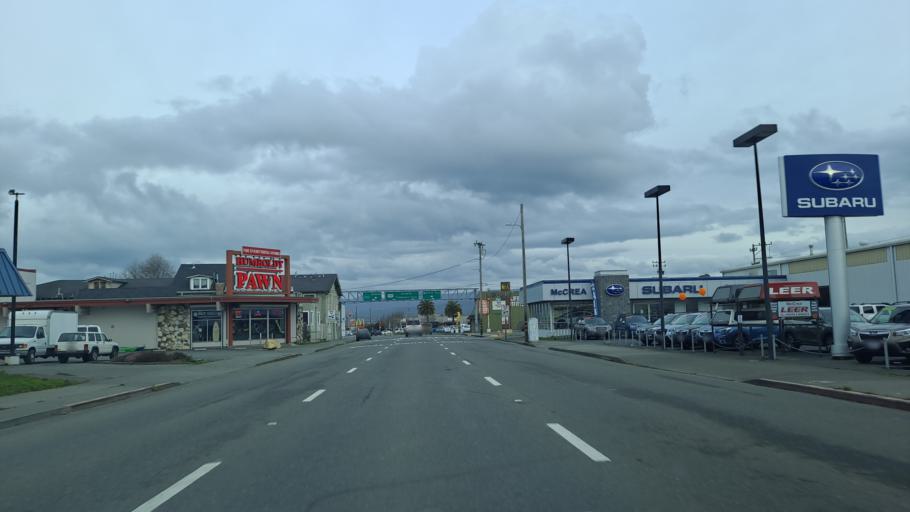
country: US
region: California
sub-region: Humboldt County
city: Eureka
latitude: 40.8033
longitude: -124.1561
